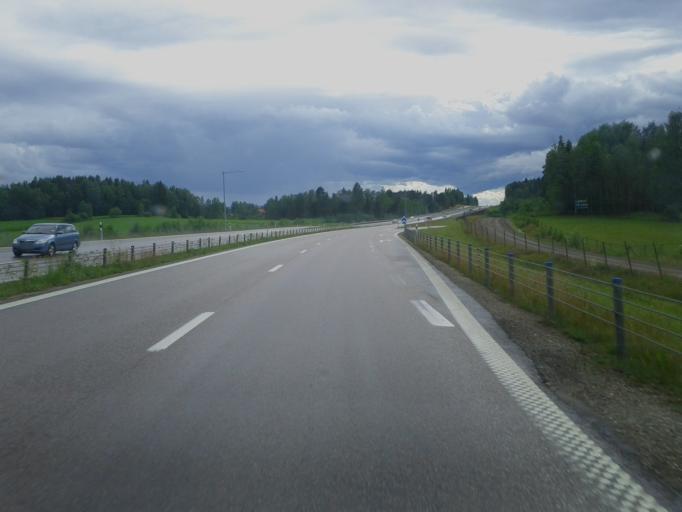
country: SE
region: Dalarna
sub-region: Borlange Kommun
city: Ornas
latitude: 60.5173
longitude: 15.5493
